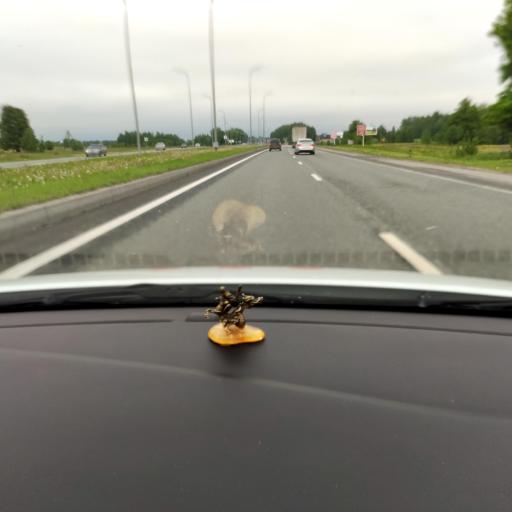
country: RU
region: Tatarstan
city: Osinovo
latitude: 55.8638
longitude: 48.7818
